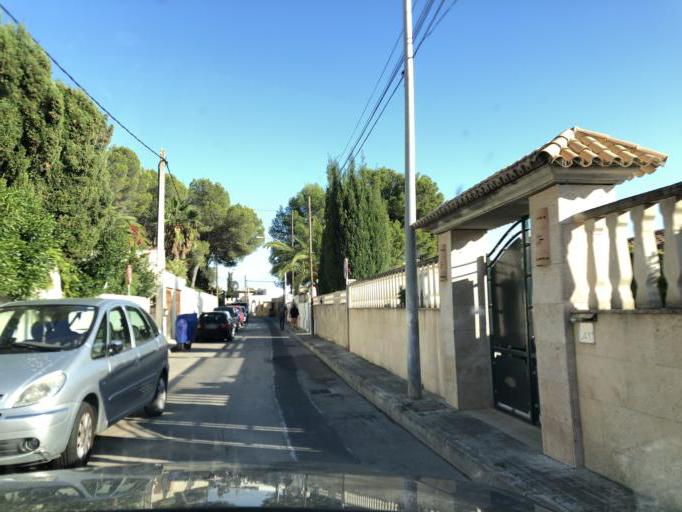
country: ES
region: Balearic Islands
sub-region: Illes Balears
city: Camp de Mar
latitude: 39.5394
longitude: 2.4417
